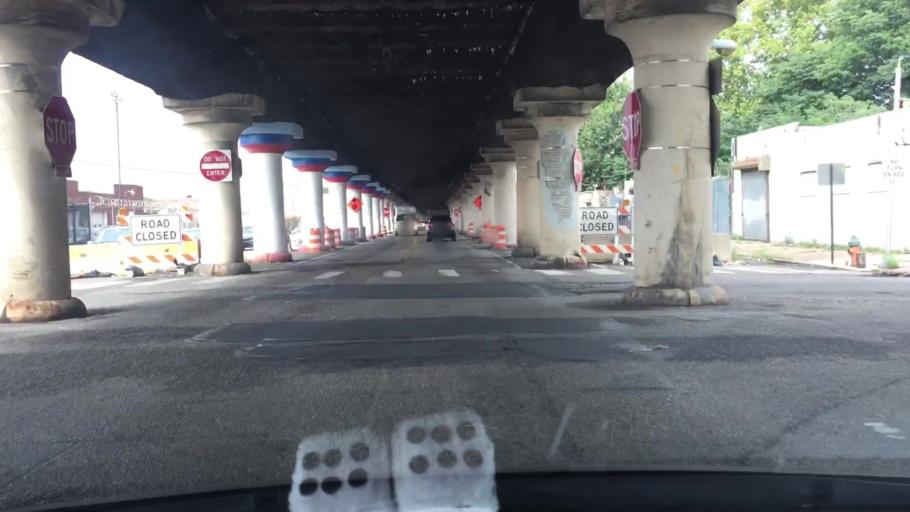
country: US
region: Pennsylvania
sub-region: Philadelphia County
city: Philadelphia
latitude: 39.9265
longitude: -75.1879
